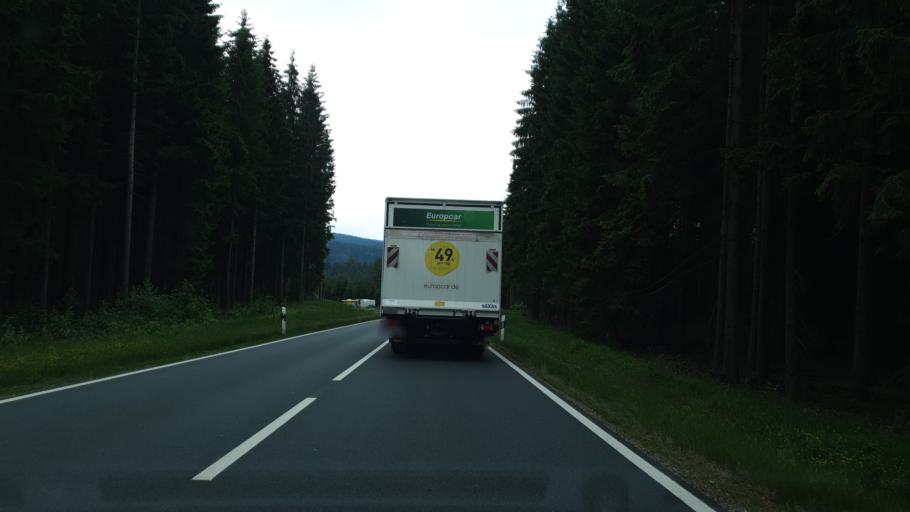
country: DE
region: Saxony
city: Tannenbergsthal
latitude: 50.4548
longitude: 12.4552
